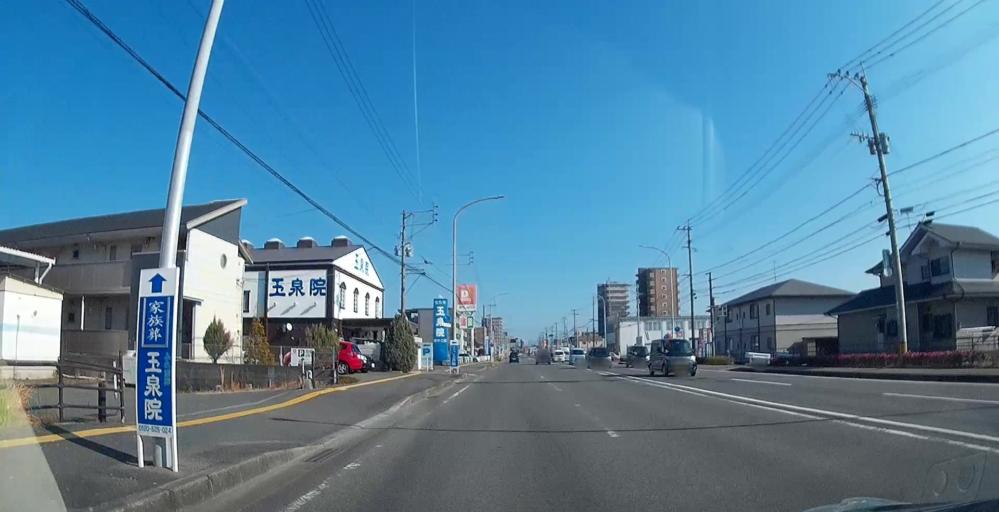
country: JP
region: Kumamoto
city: Kumamoto
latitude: 32.7760
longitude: 130.6747
